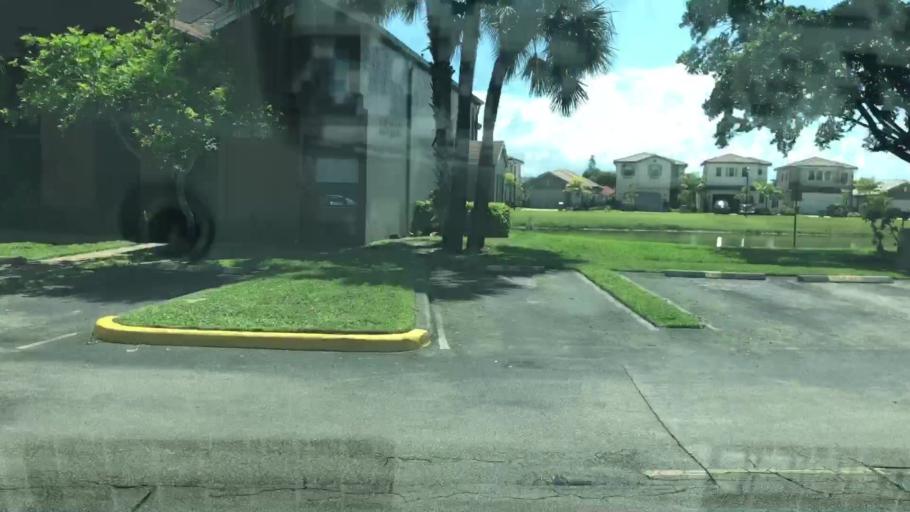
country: US
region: Florida
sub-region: Broward County
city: Sunshine Ranches
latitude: 26.0031
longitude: -80.2997
